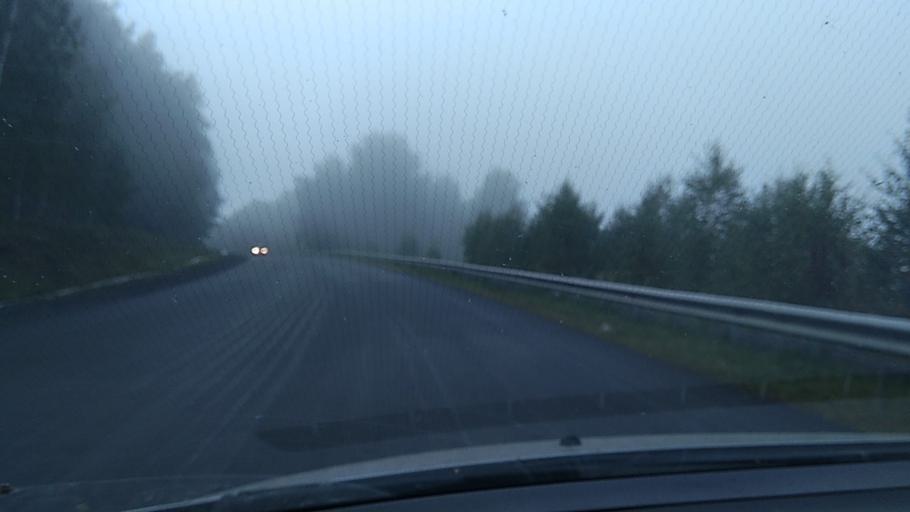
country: RU
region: Chelyabinsk
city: Karabash
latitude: 55.3386
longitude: 60.2405
